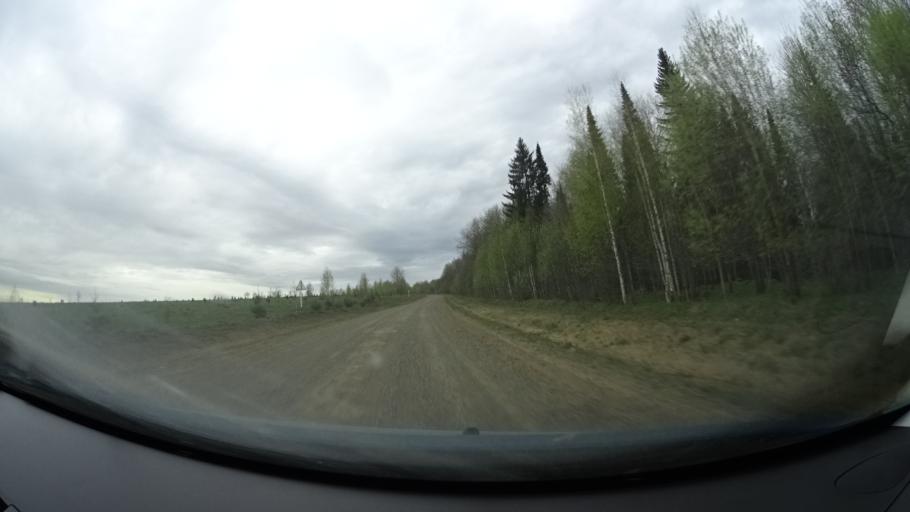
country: RU
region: Perm
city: Kuyeda
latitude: 56.6043
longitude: 55.7135
